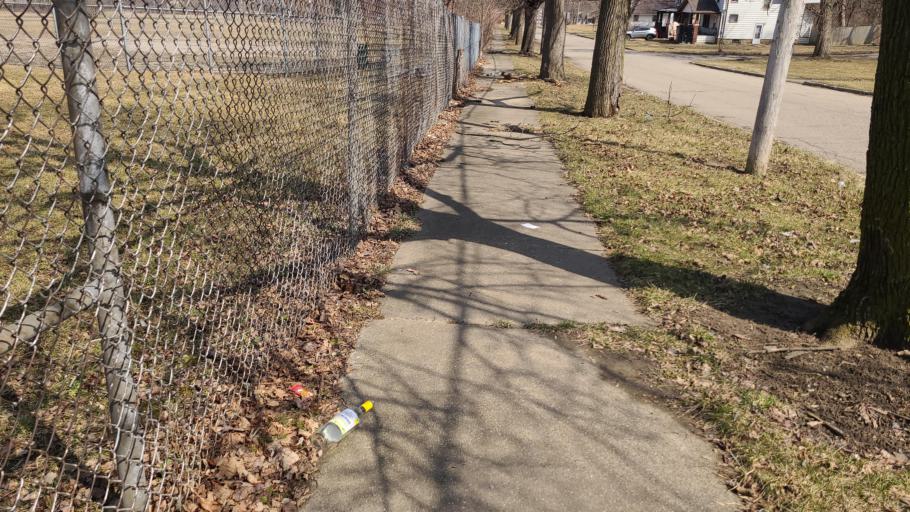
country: US
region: Michigan
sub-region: Genesee County
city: Flint
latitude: 43.0350
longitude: -83.7004
